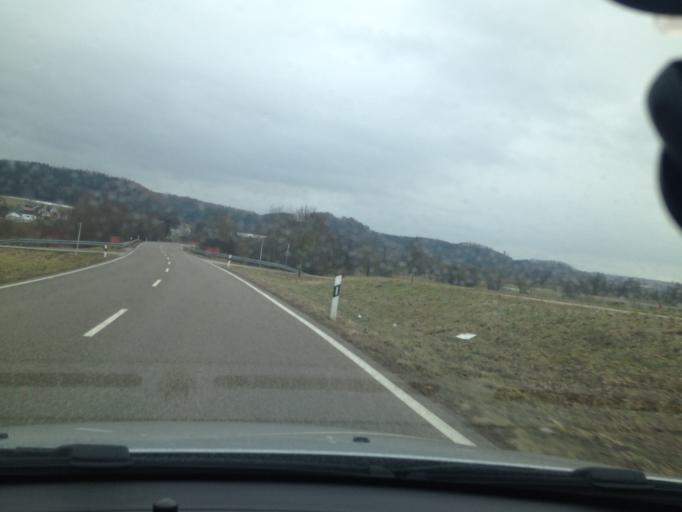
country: DE
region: Bavaria
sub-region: Swabia
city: Altenmunster
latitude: 48.4366
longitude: 10.5905
